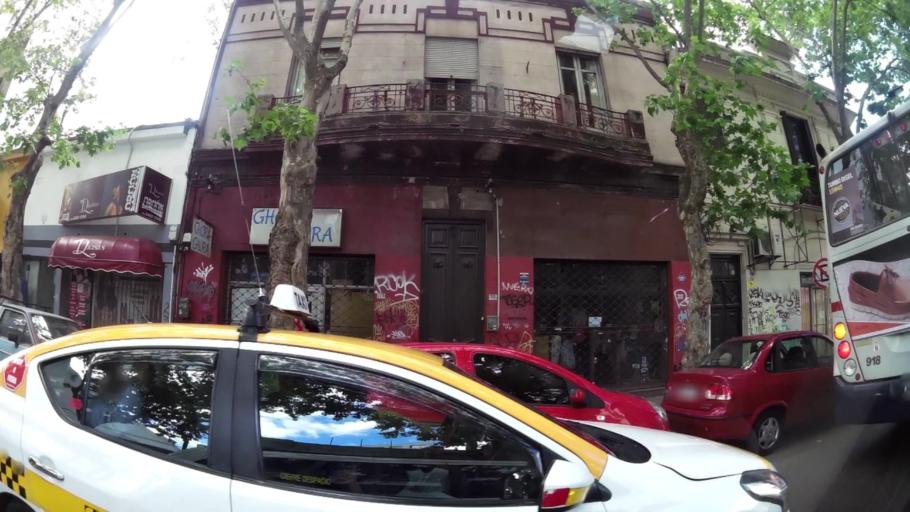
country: UY
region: Montevideo
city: Montevideo
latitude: -34.9023
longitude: -56.1732
